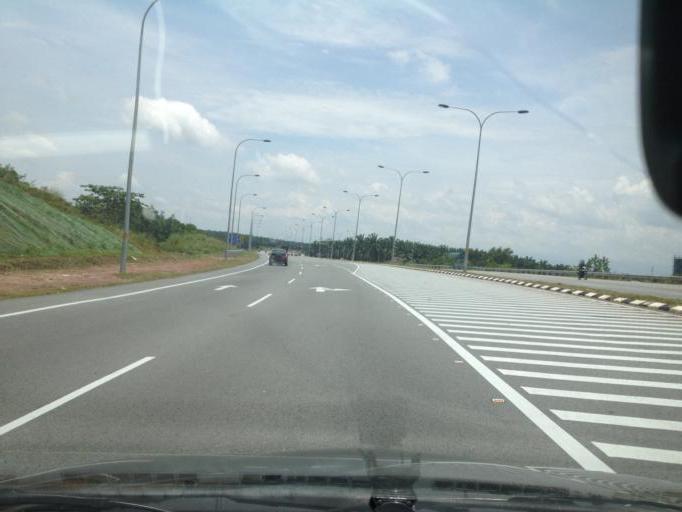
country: MY
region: Kedah
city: Sungai Petani
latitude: 5.6116
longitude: 100.5658
